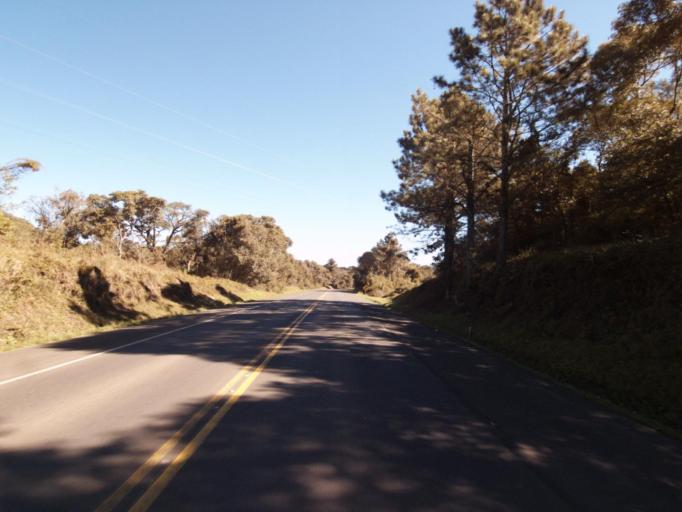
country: BR
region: Santa Catarina
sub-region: Joacaba
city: Joacaba
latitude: -27.1083
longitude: -51.6386
